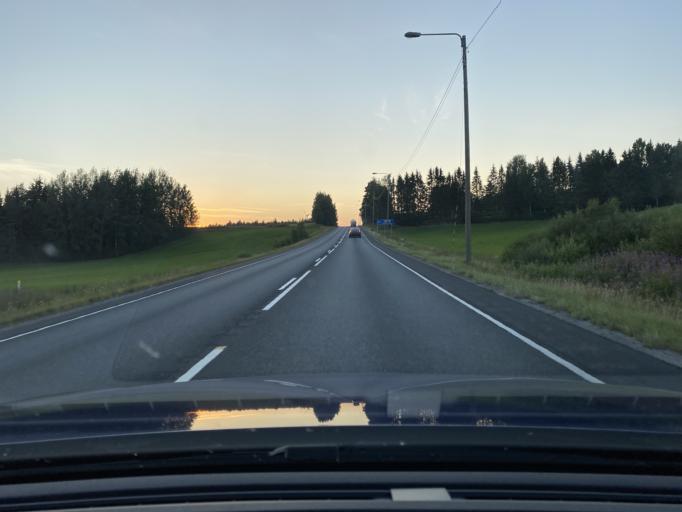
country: FI
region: Pirkanmaa
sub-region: Luoteis-Pirkanmaa
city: Ikaalinen
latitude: 61.7690
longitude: 23.0154
